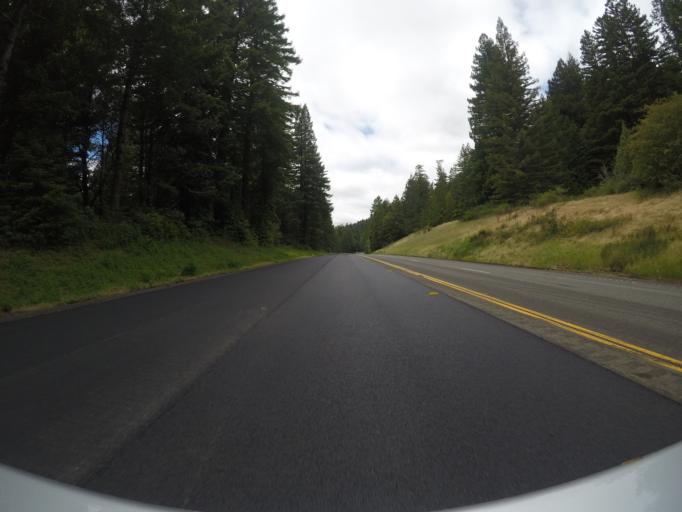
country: US
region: California
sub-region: Humboldt County
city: Redway
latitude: 40.3069
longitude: -123.9032
